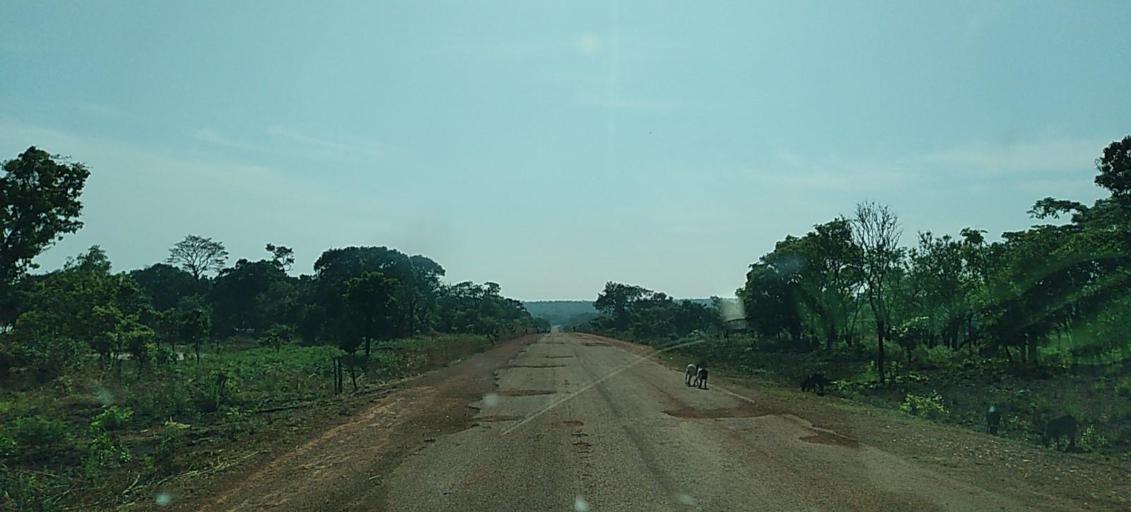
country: ZM
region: North-Western
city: Mwinilunga
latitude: -11.7863
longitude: 25.0312
